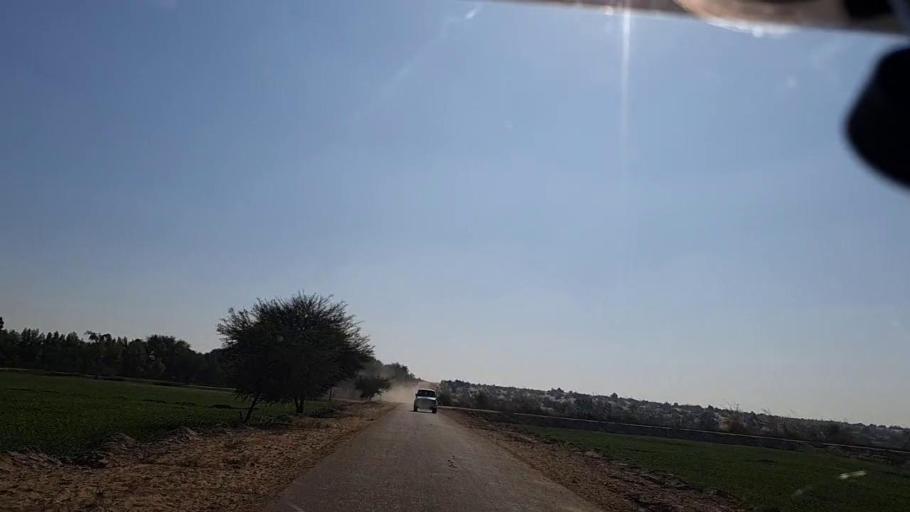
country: PK
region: Sindh
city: Khanpur
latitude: 27.5673
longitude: 69.3888
